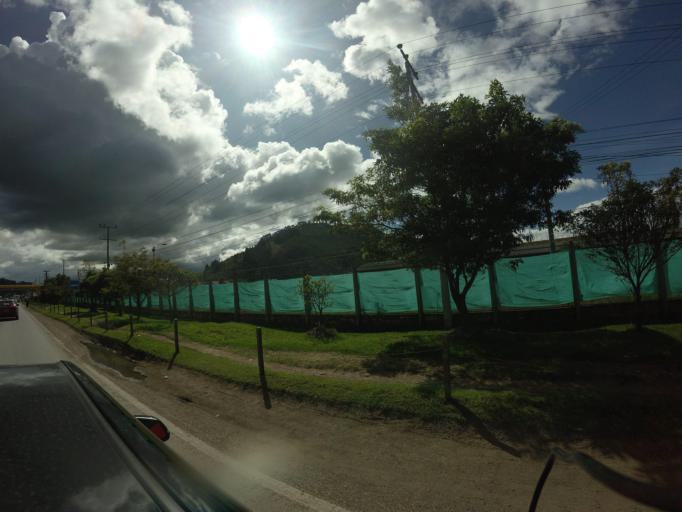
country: CO
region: Cundinamarca
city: Sopo
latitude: 4.9428
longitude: -73.9600
